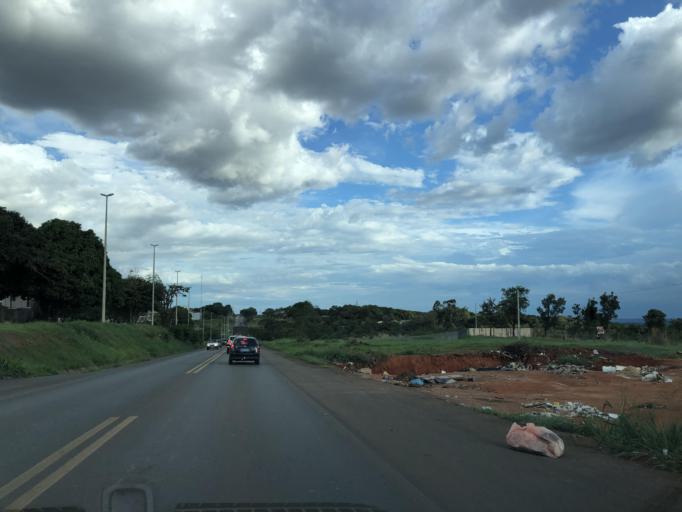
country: BR
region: Goias
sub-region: Luziania
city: Luziania
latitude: -16.0367
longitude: -48.0691
